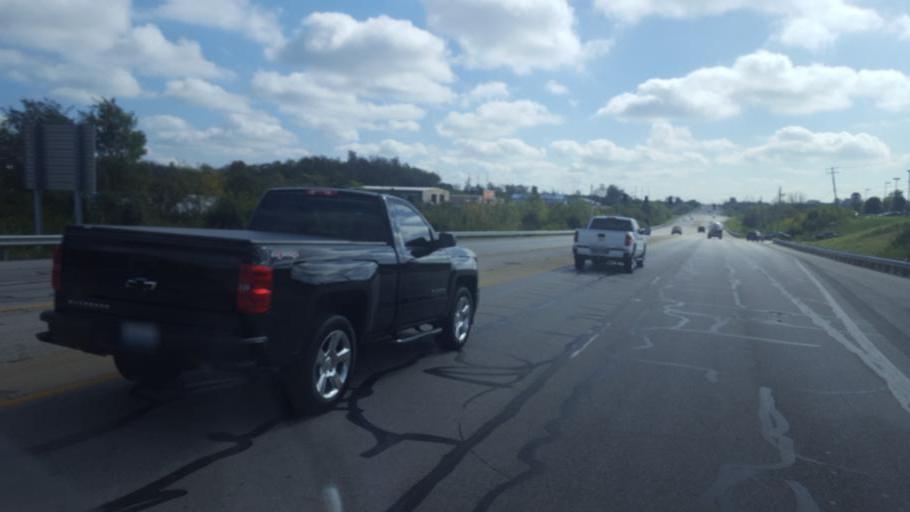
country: US
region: Ohio
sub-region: Brown County
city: Aberdeen
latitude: 38.6285
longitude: -83.7917
